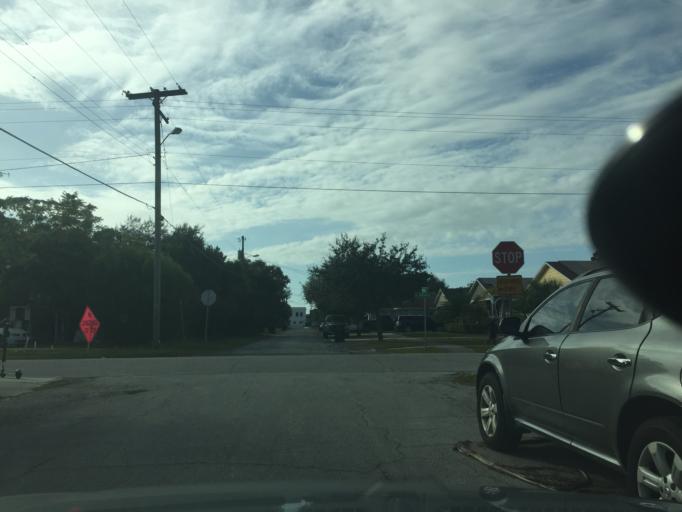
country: US
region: Florida
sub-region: Hillsborough County
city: Tampa
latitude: 27.9492
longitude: -82.4807
